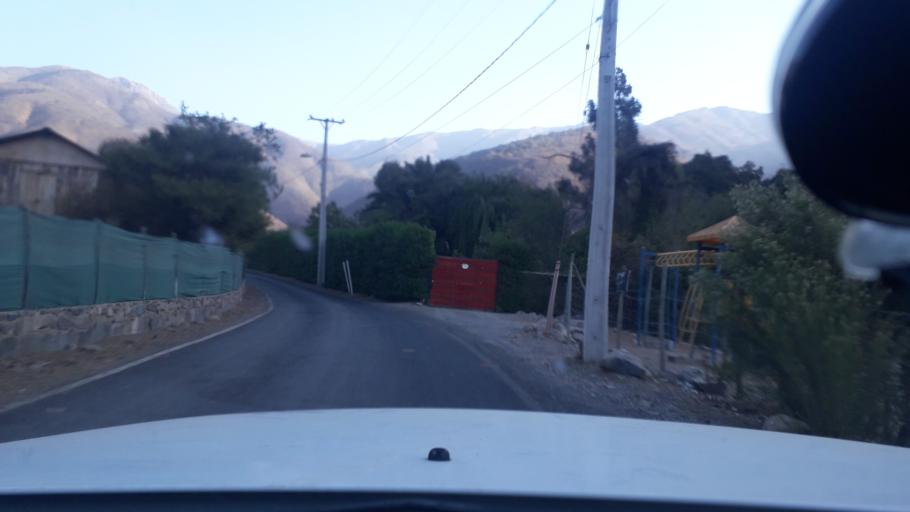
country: CL
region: Valparaiso
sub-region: Provincia de Marga Marga
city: Limache
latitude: -33.0623
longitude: -71.1172
